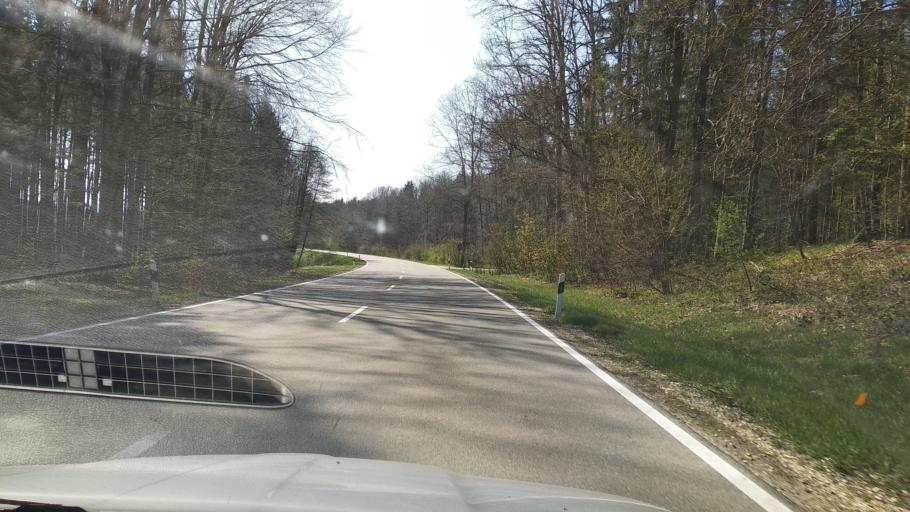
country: DE
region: Bavaria
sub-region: Swabia
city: Erkheim
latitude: 48.0470
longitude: 10.3812
